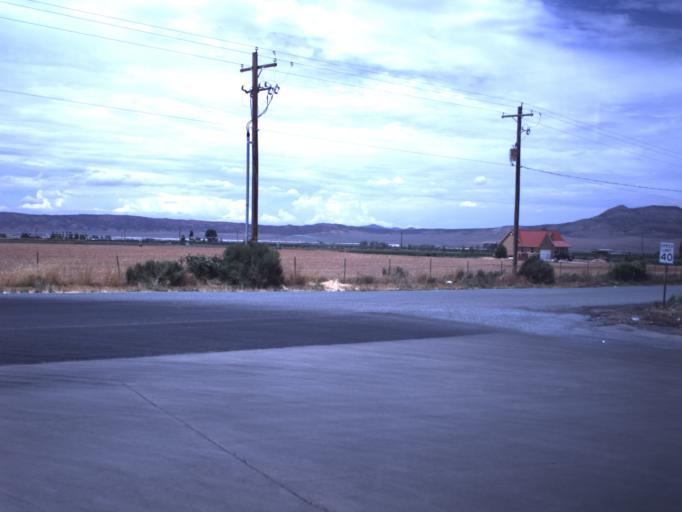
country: US
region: Utah
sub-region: Iron County
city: Parowan
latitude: 37.8615
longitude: -112.8301
